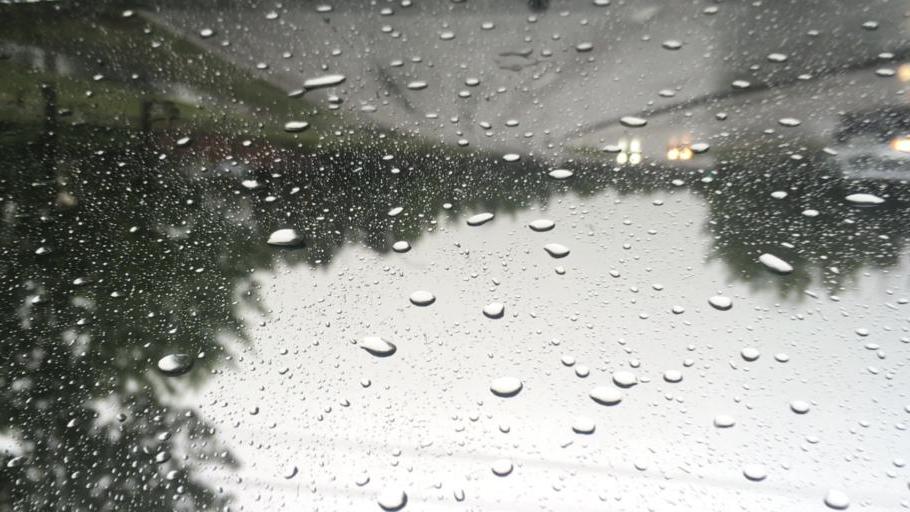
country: CA
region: Alberta
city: Edmonton
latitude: 53.4619
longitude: -113.5390
